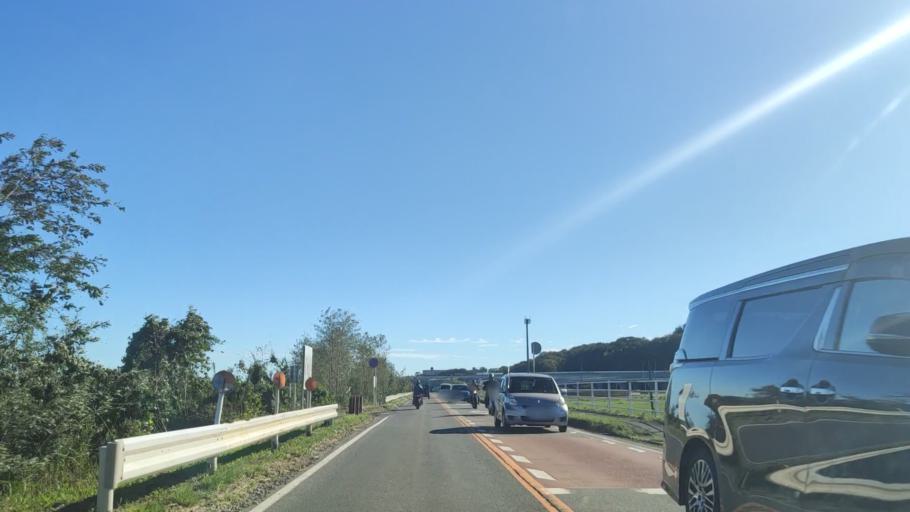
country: JP
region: Kanagawa
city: Zama
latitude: 35.4972
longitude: 139.3708
